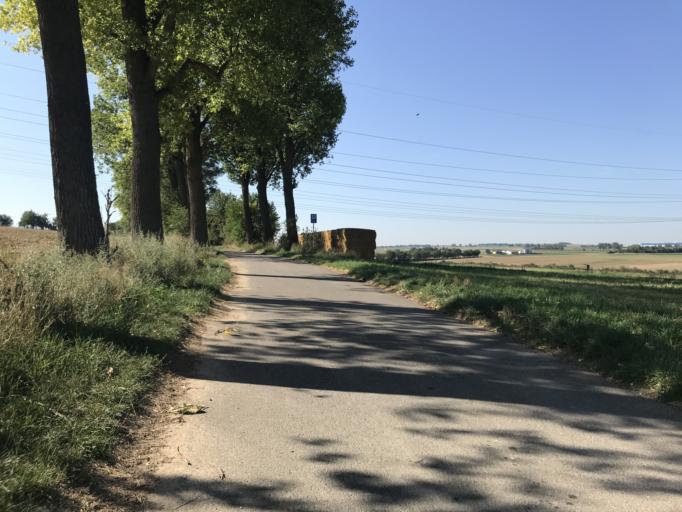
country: DE
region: Rheinland-Pfalz
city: Mainz
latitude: 49.9522
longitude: 8.2808
